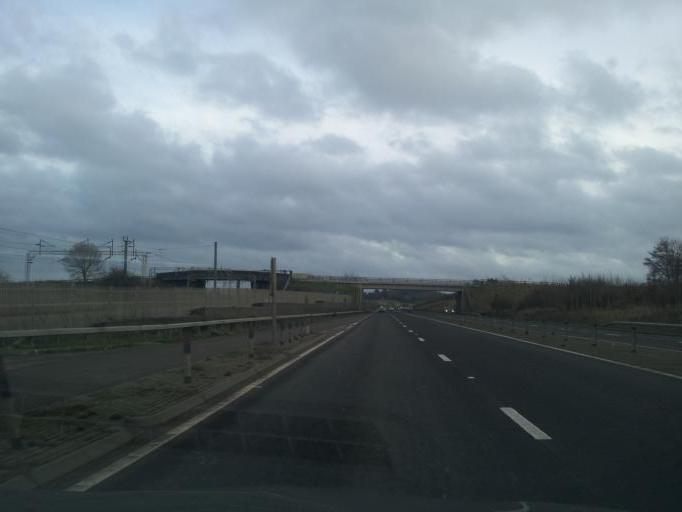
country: GB
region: England
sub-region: Milton Keynes
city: Water Eaton
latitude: 51.9441
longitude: -0.7101
